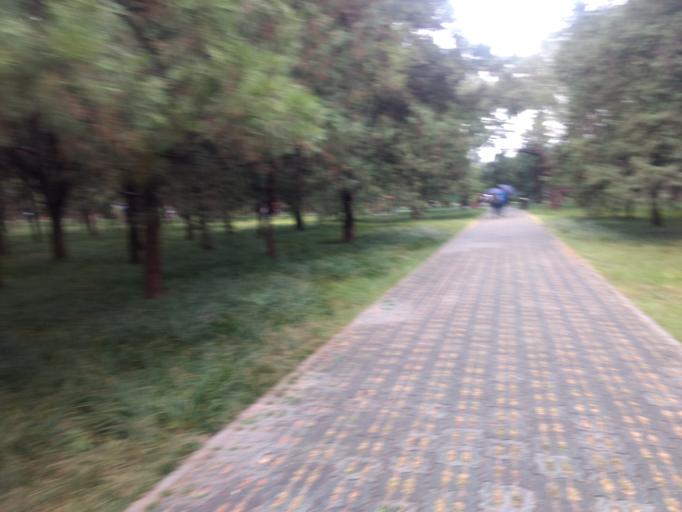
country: CN
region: Beijing
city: Longtan
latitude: 39.8793
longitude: 116.4018
